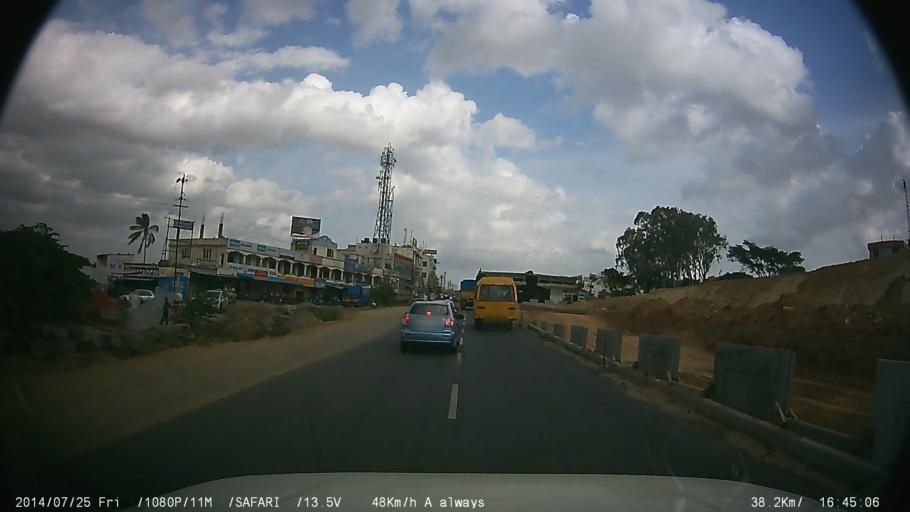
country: IN
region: Tamil Nadu
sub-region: Krishnagiri
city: Hosur
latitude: 12.7420
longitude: 77.8193
